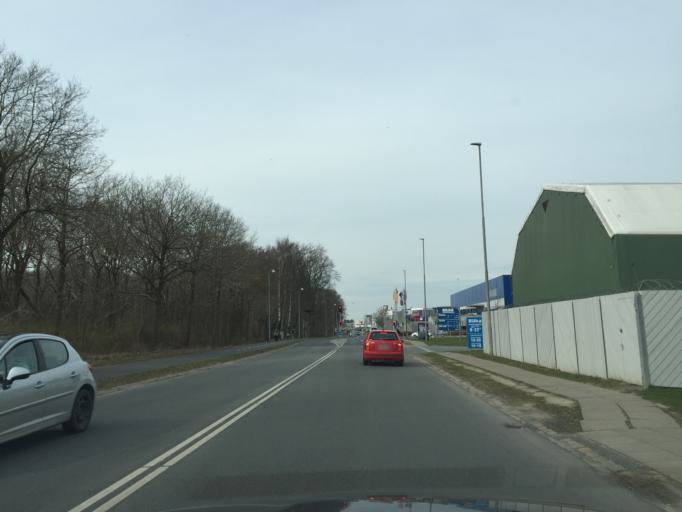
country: DK
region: South Denmark
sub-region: Odense Kommune
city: Neder Holluf
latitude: 55.3784
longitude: 10.4299
